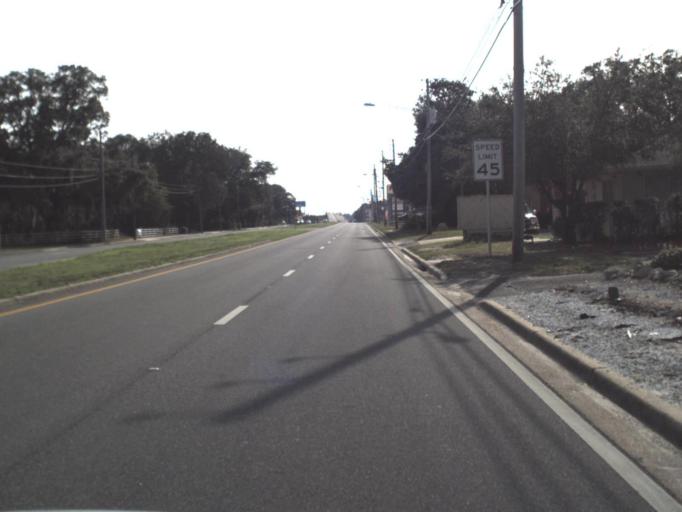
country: US
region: Florida
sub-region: Bay County
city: Parker
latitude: 30.1155
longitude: -85.5985
